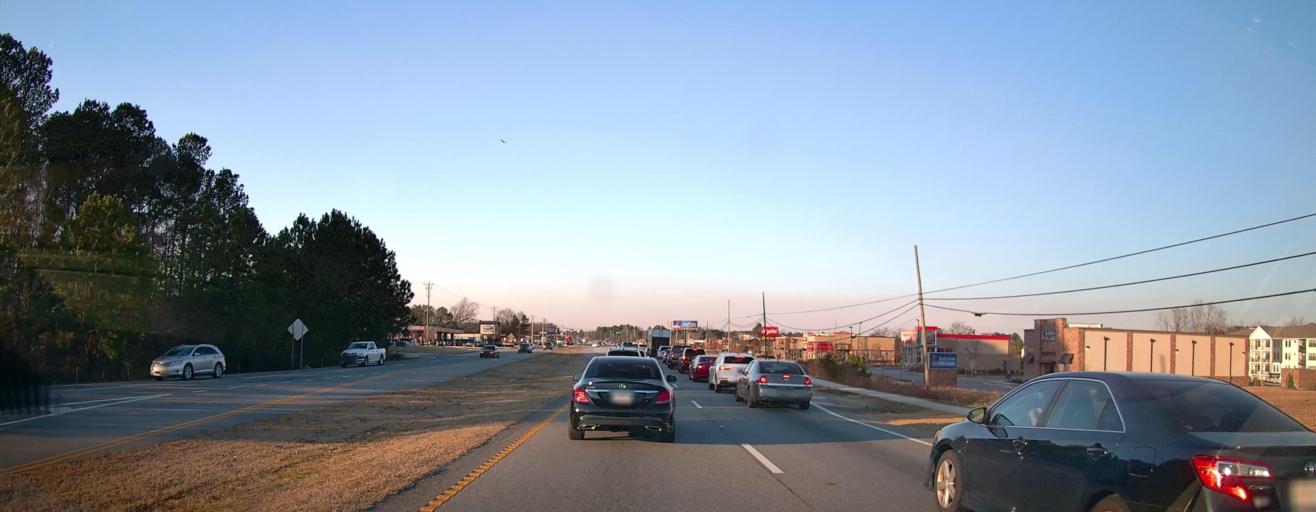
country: US
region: Georgia
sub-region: Fulton County
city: Fairburn
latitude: 33.5367
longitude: -84.5769
